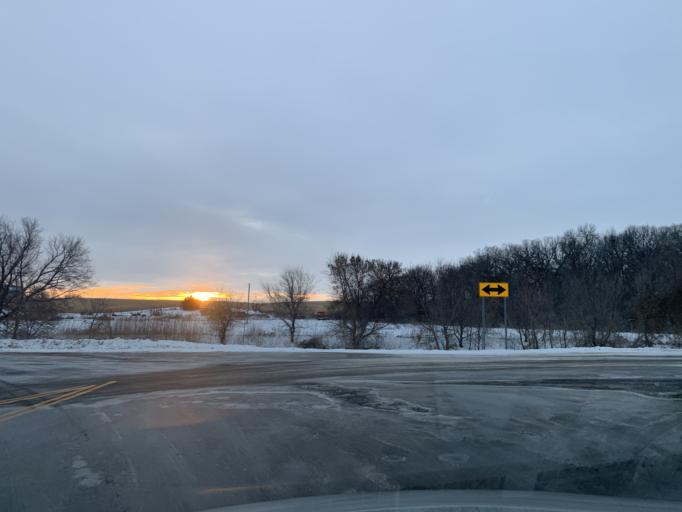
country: US
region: Minnesota
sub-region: Carver County
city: Cologne
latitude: 44.7702
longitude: -93.7671
